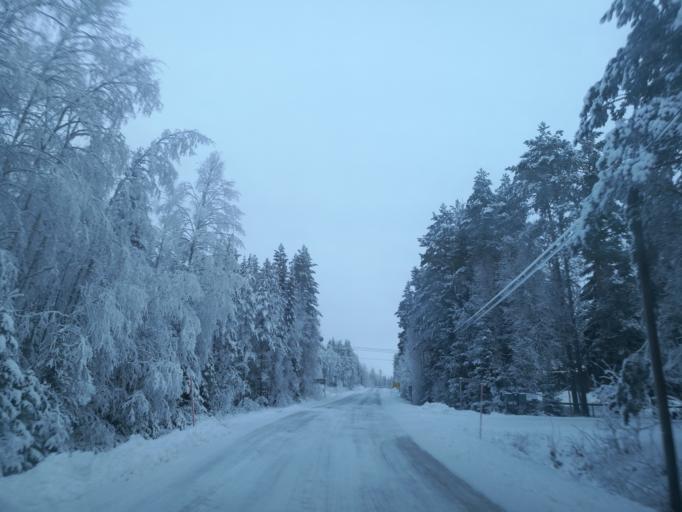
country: NO
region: Hedmark
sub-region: Grue
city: Kirkenaer
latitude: 60.4193
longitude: 12.4506
